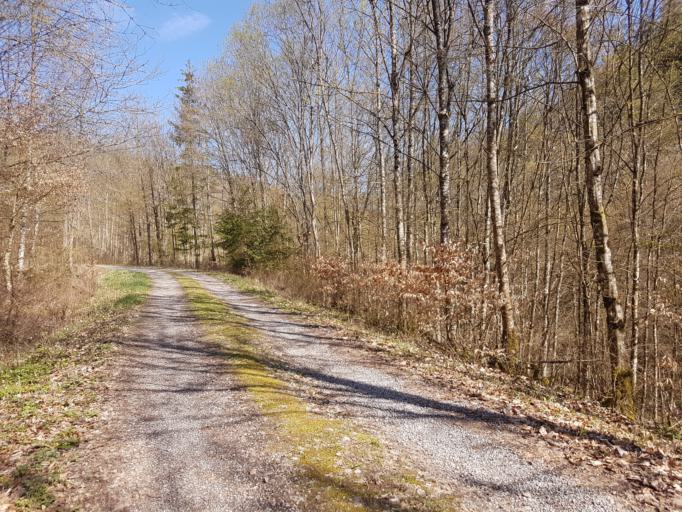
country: DE
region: Baden-Wuerttemberg
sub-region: Regierungsbezirk Stuttgart
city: Jagsthausen
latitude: 49.3391
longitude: 9.4914
